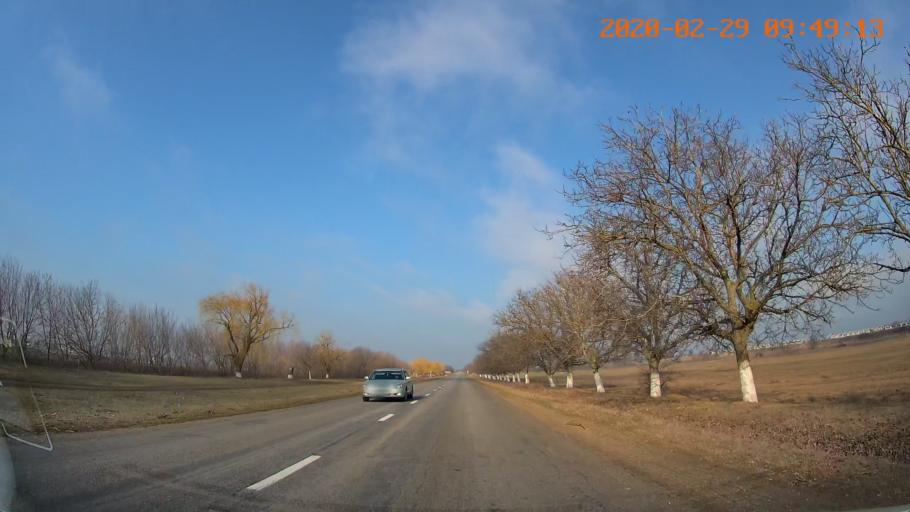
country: MD
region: Telenesti
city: Crasnoe
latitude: 46.6959
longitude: 29.7751
